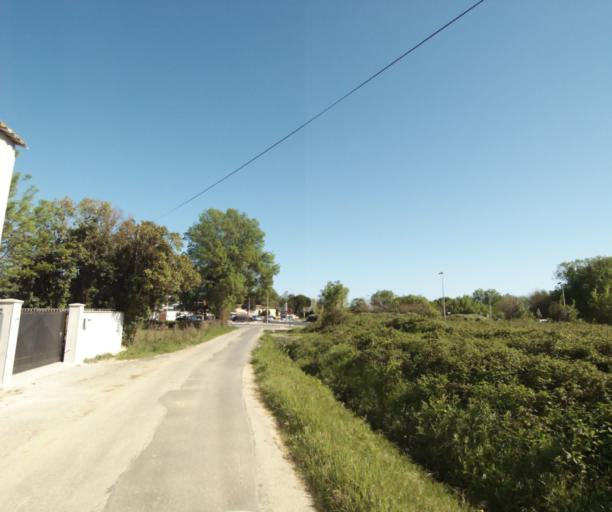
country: FR
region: Languedoc-Roussillon
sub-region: Departement de l'Herault
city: Lattes
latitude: 43.5733
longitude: 3.8925
